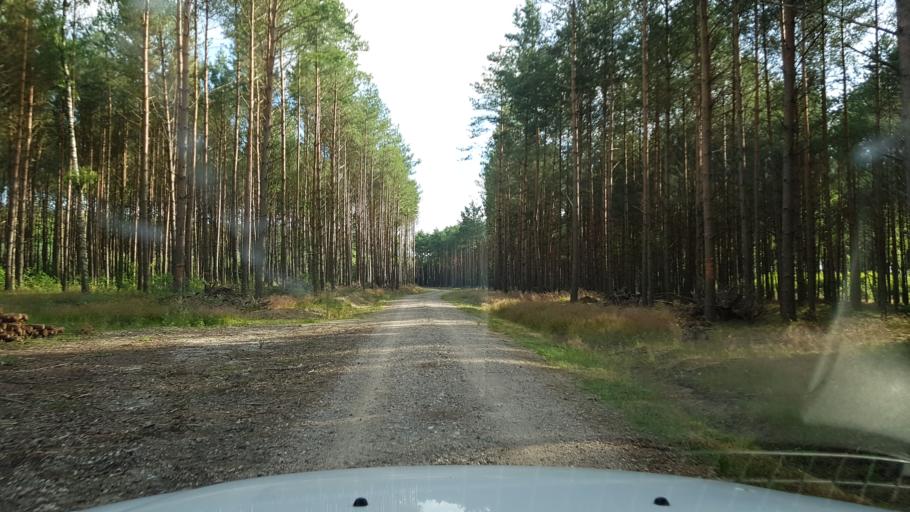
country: PL
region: West Pomeranian Voivodeship
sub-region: Powiat kolobrzeski
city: Grzybowo
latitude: 54.1035
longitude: 15.5405
